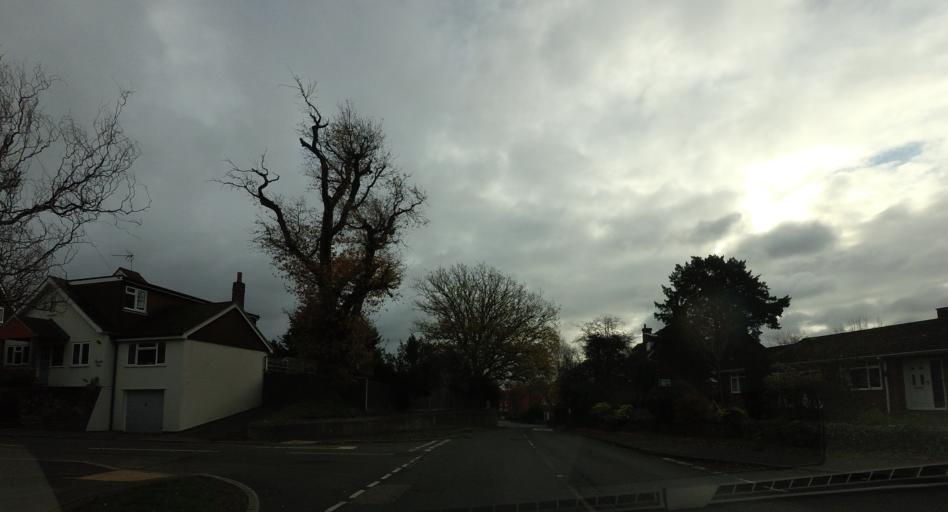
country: GB
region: England
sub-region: Kent
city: Paddock Wood
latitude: 51.1383
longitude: 0.4304
